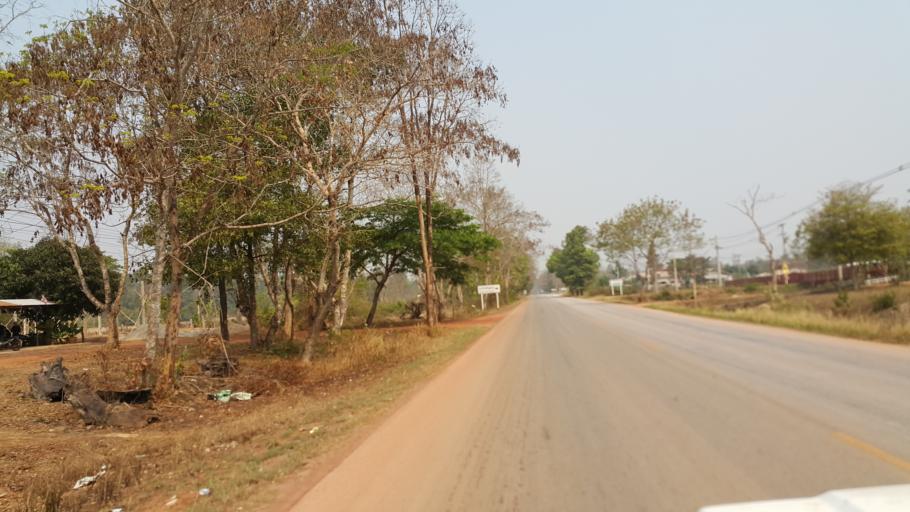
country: TH
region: Nakhon Phanom
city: Ban Phaeng
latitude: 17.8362
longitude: 104.2656
